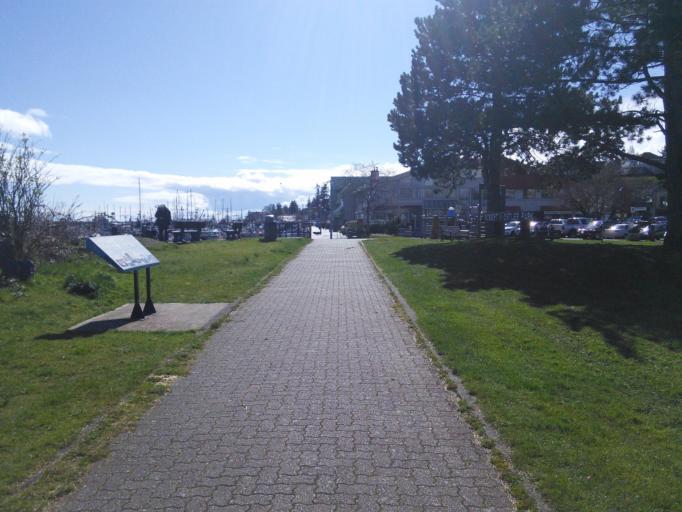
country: CA
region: British Columbia
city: Campbell River
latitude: 50.0249
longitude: -125.2402
